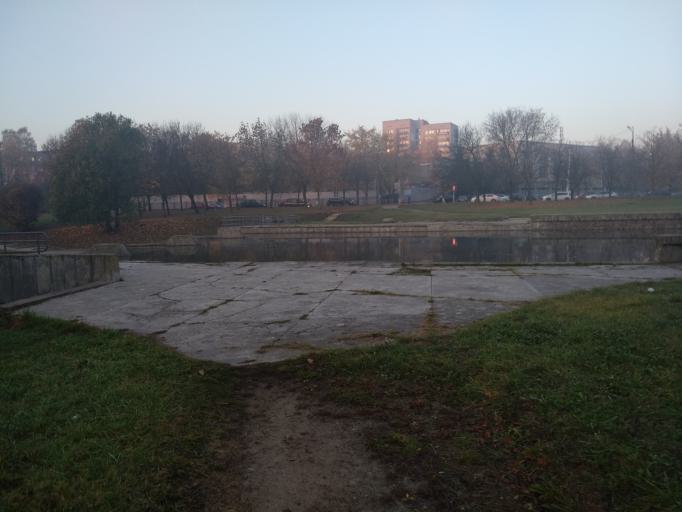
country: BY
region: Minsk
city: Borovlyany
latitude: 53.9471
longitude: 27.6426
